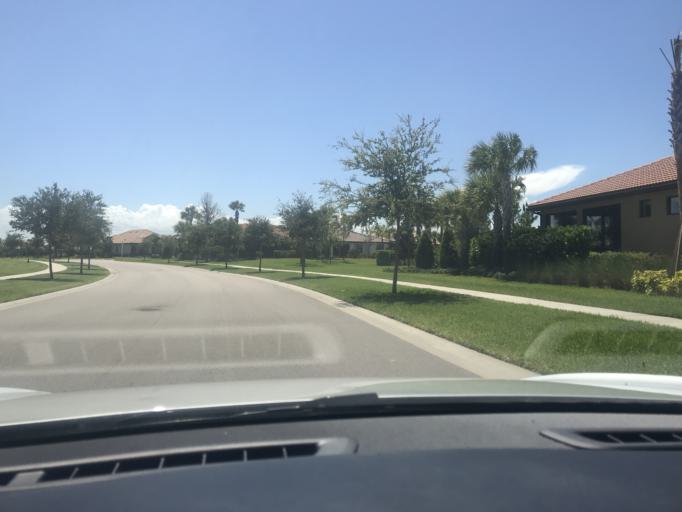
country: US
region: Florida
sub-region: Indian River County
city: Gifford
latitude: 27.6897
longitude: -80.4282
